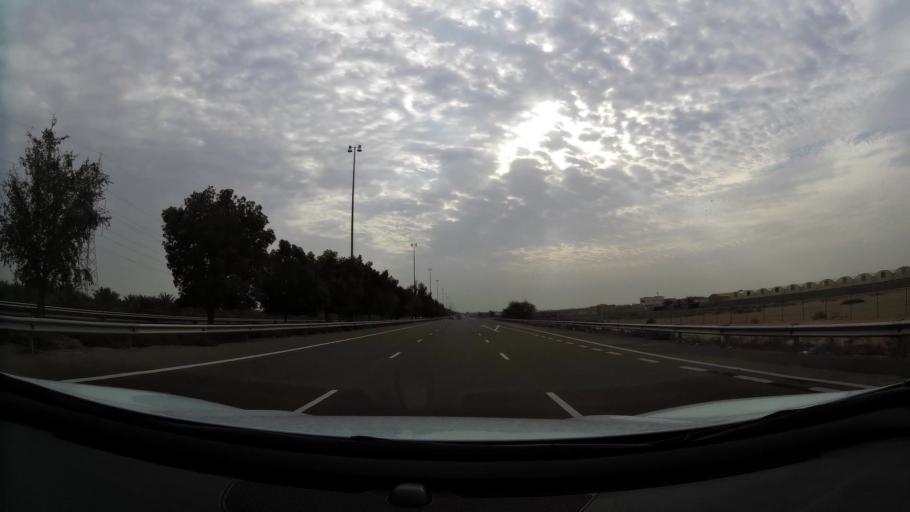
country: AE
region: Abu Dhabi
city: Abu Dhabi
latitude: 24.1897
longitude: 55.0133
